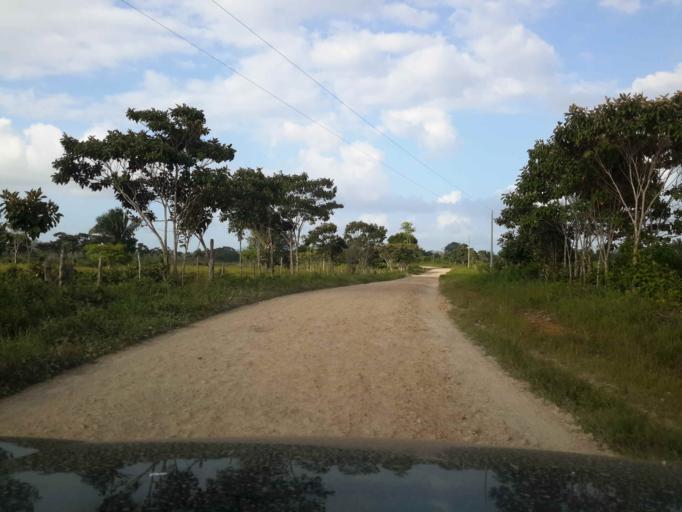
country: CR
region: Alajuela
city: Los Chiles
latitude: 11.1256
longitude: -84.6089
